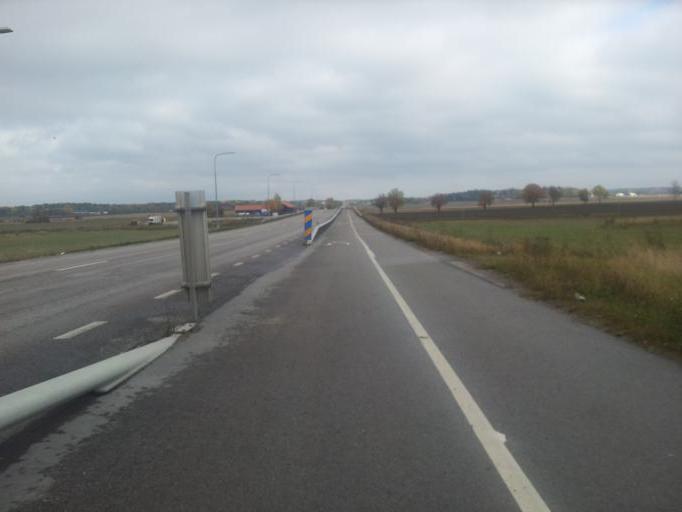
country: SE
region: Uppsala
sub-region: Uppsala Kommun
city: Uppsala
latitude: 59.8799
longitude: 17.6847
